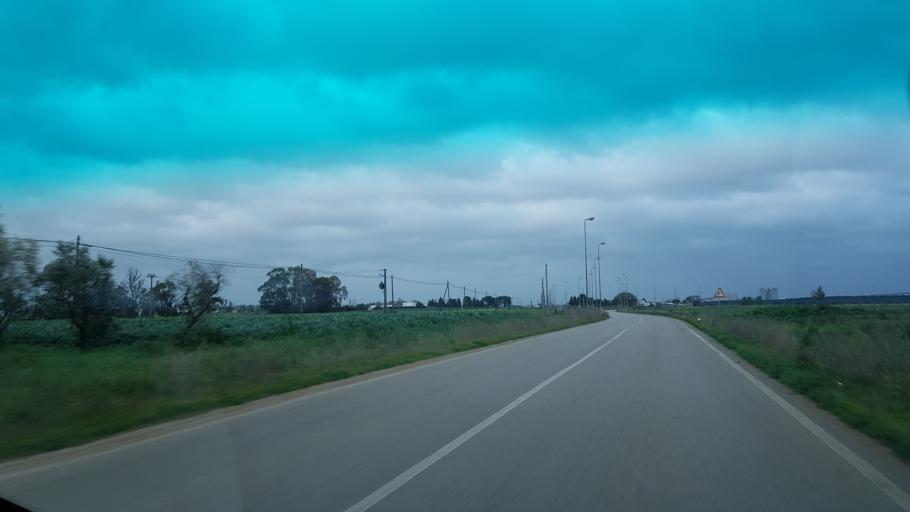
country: IT
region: Apulia
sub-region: Provincia di Brindisi
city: Tuturano
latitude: 40.5594
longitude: 18.0046
